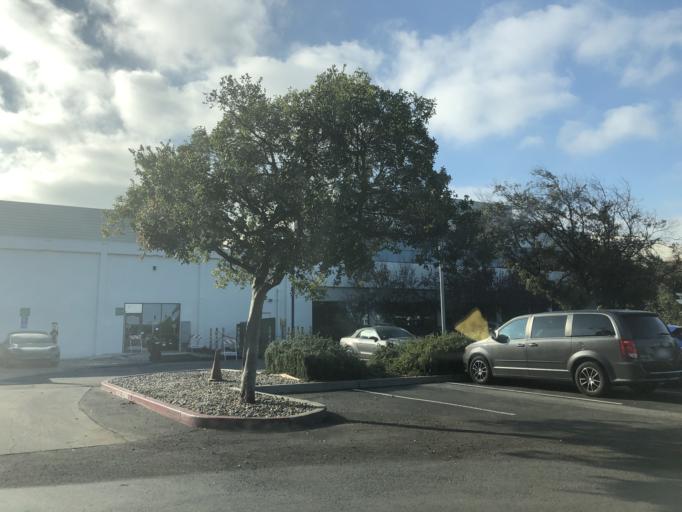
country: US
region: California
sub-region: Santa Clara County
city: Sunnyvale
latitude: 37.3850
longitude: -122.0094
